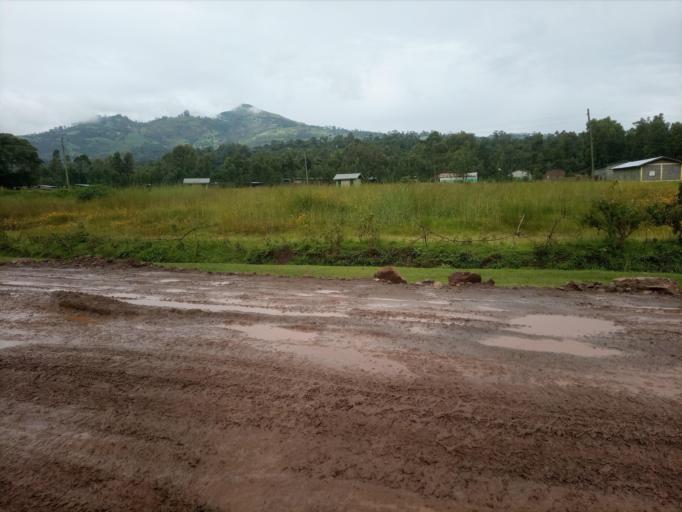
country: ET
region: Southern Nations, Nationalities, and People's Region
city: K'olito
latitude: 7.2986
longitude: 37.9258
